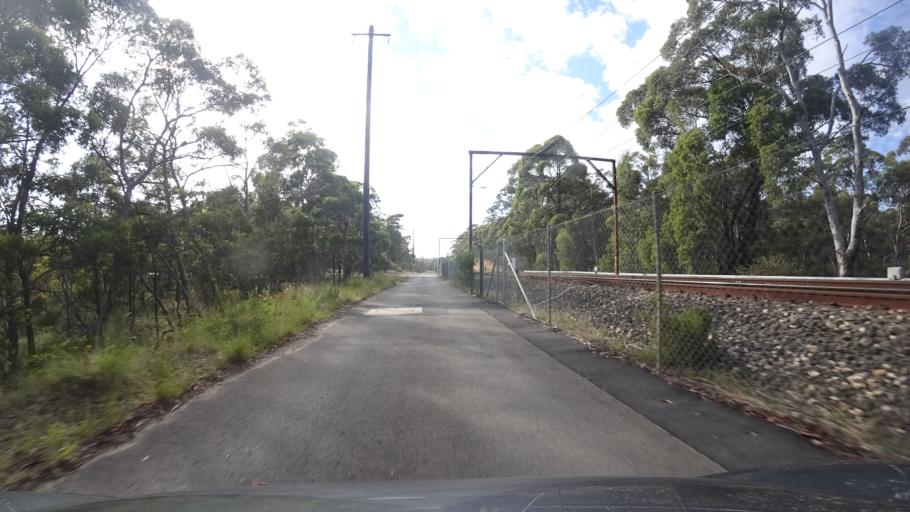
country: AU
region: New South Wales
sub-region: Lithgow
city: Lithgow
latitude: -33.4747
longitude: 150.2419
